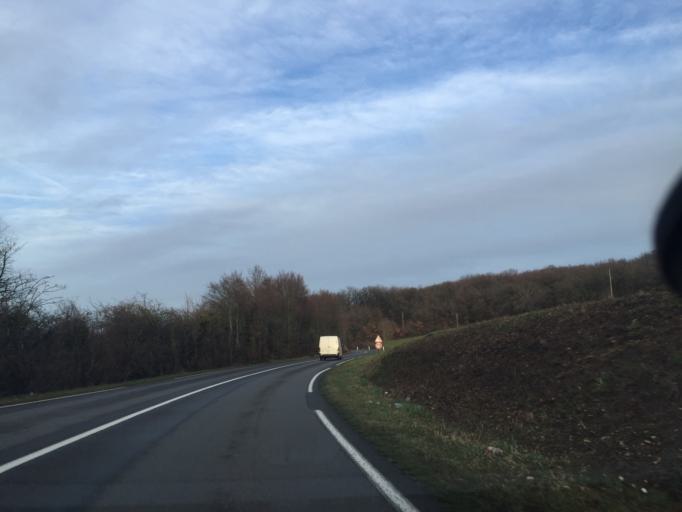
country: FR
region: Rhone-Alpes
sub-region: Departement de l'Isere
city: Vaulx-Milieu
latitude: 45.6081
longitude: 5.1686
